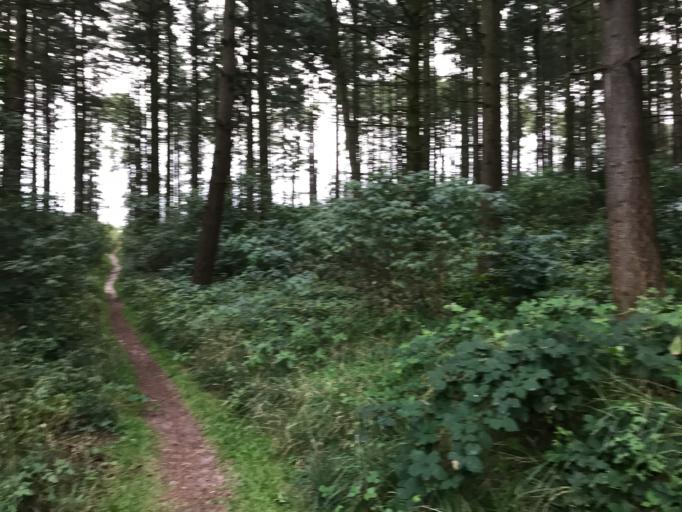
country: DE
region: Mecklenburg-Vorpommern
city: Loddin
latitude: 54.0326
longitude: 14.0412
